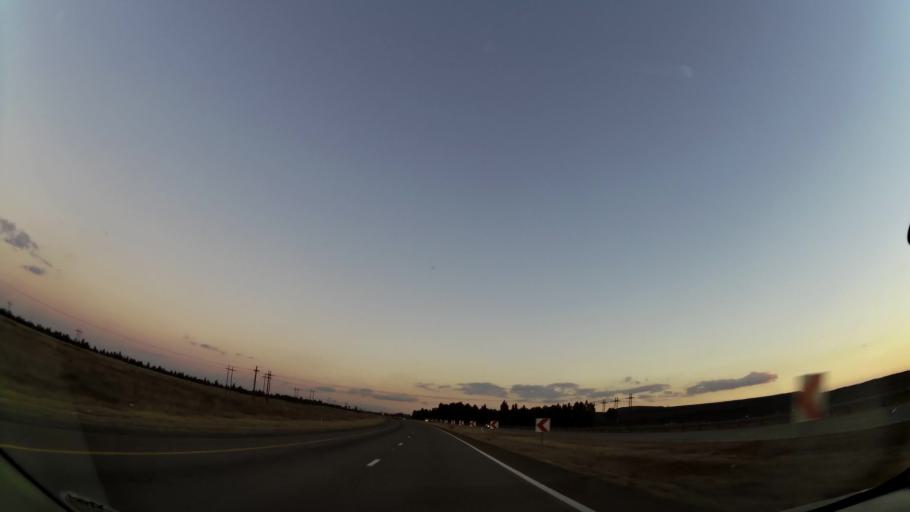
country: ZA
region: Mpumalanga
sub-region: Nkangala District Municipality
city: Witbank
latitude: -25.9510
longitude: 29.1972
